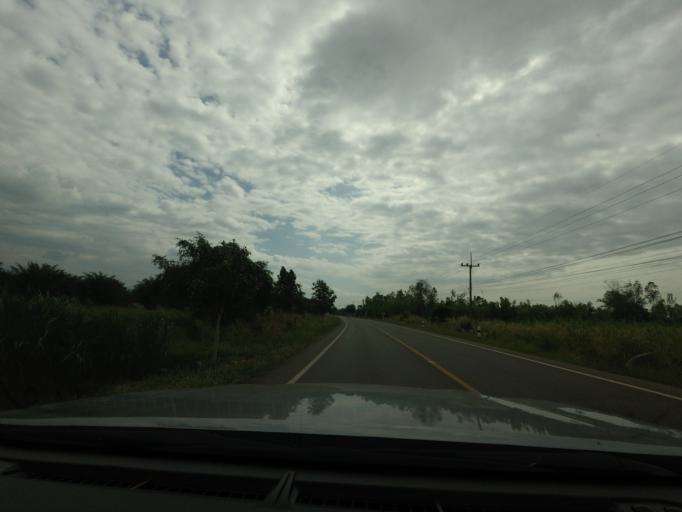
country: TH
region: Phitsanulok
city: Noen Maprang
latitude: 16.6084
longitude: 100.6202
